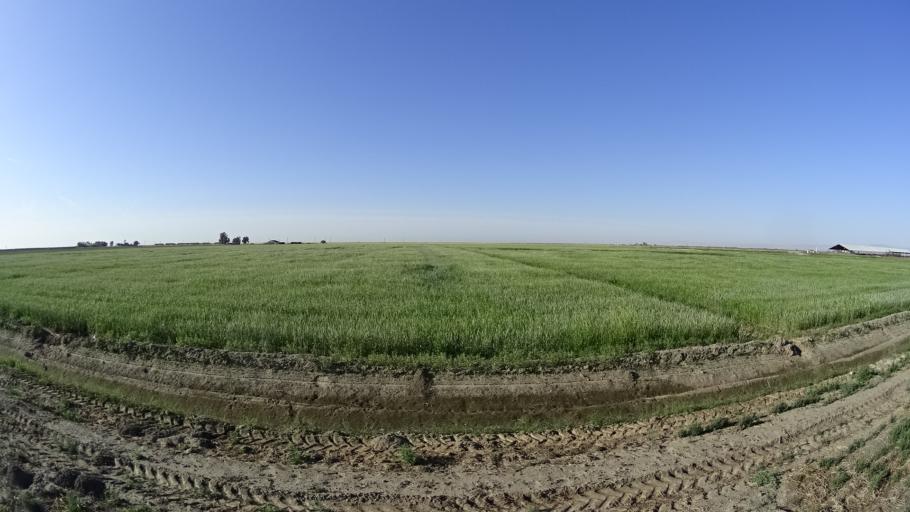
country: US
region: California
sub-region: Kings County
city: Stratford
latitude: 36.1673
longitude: -119.7913
